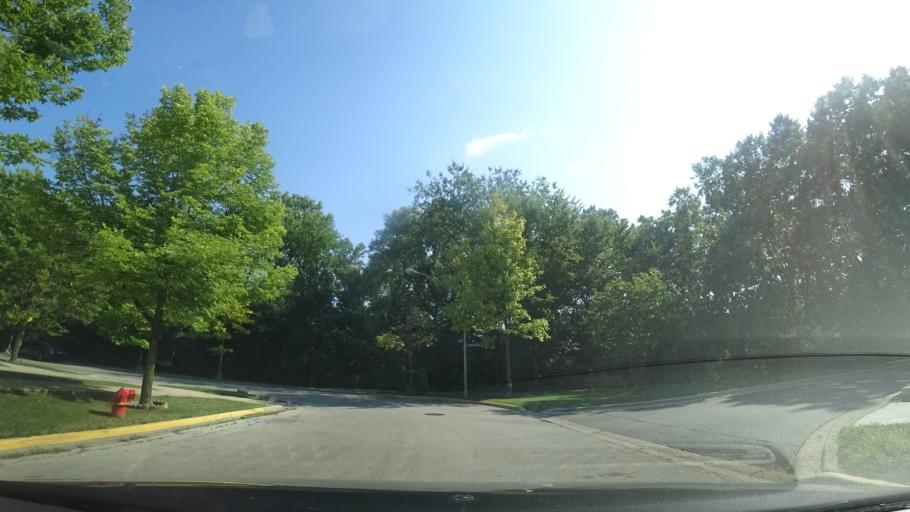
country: US
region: Illinois
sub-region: Cook County
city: Lincolnwood
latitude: 41.9779
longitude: -87.7369
